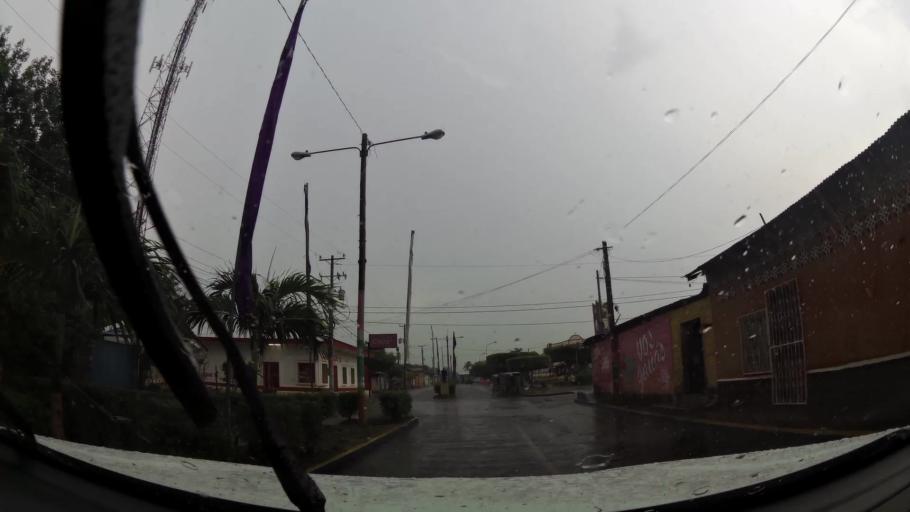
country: NI
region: Leon
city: Telica
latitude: 12.5215
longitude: -86.8611
